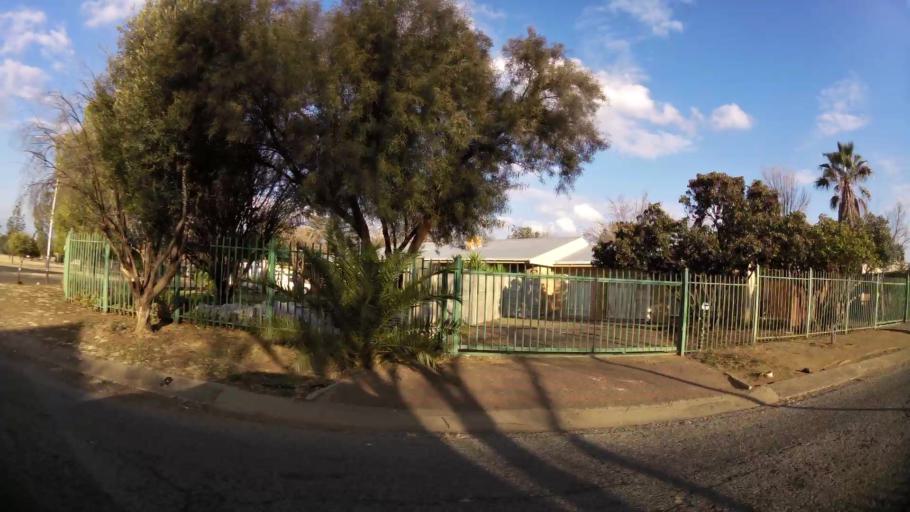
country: ZA
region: Orange Free State
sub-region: Mangaung Metropolitan Municipality
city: Bloemfontein
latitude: -29.1455
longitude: 26.1850
